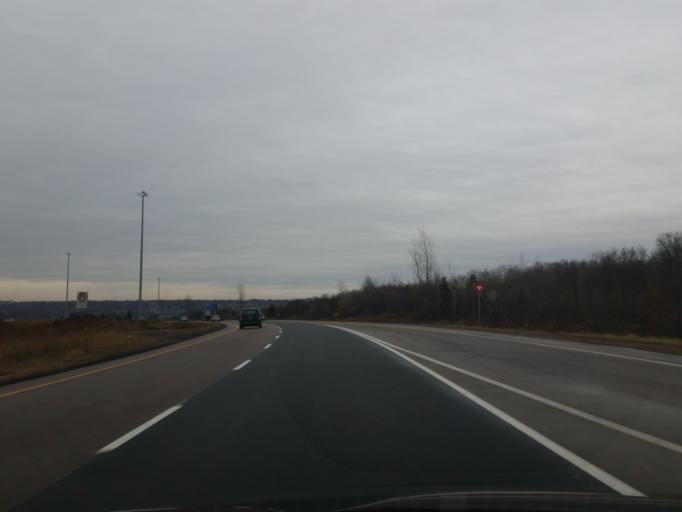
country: CA
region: Quebec
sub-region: Capitale-Nationale
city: Saint-Augustin-de-Desmaures
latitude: 46.7522
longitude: -71.4174
